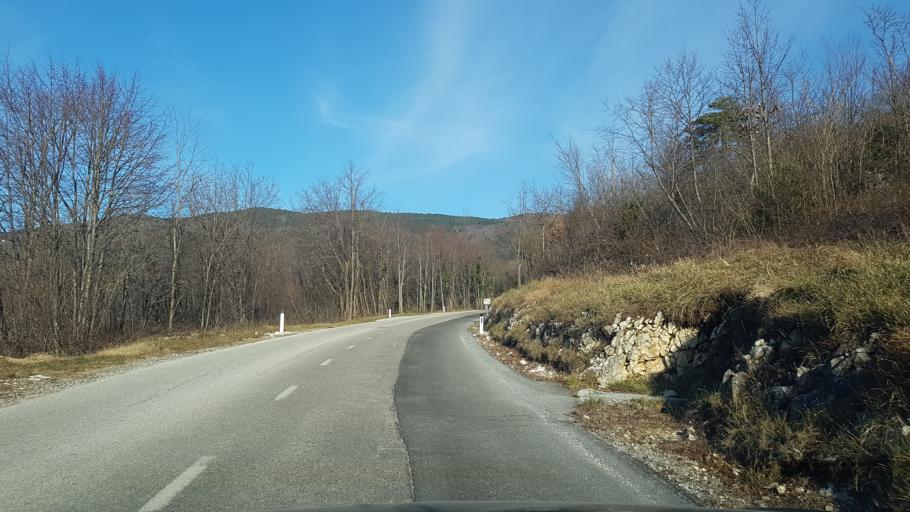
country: SI
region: Nova Gorica
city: Kromberk
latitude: 46.0037
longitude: 13.6871
